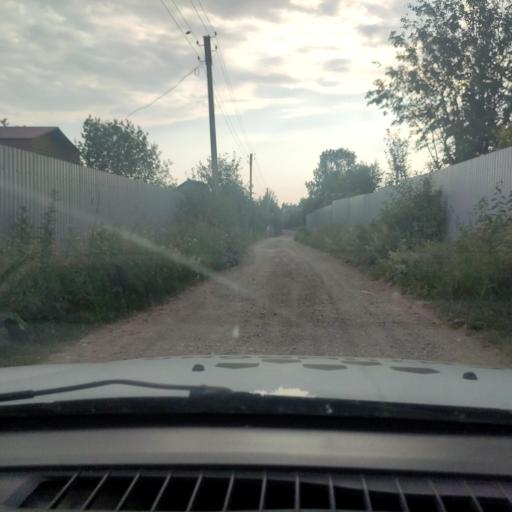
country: RU
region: Perm
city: Polazna
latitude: 58.1713
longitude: 56.3623
